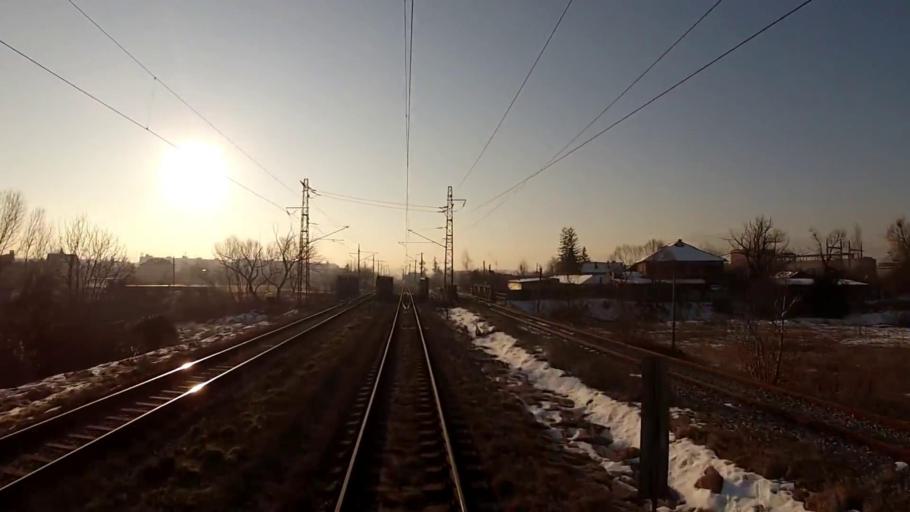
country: BG
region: Sofiya
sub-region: Obshtina Bozhurishte
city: Bozhurishte
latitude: 42.7489
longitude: 23.2518
